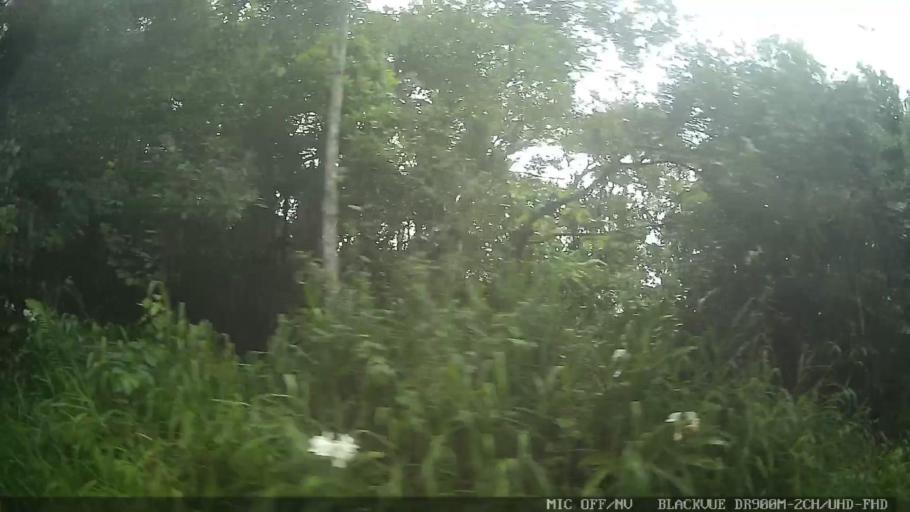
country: BR
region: Sao Paulo
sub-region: Ribeirao Pires
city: Ribeirao Pires
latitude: -23.6941
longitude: -46.3325
